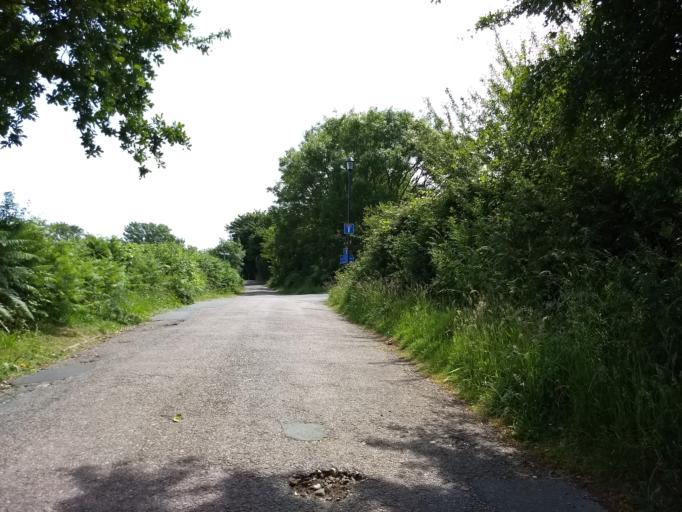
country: GB
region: England
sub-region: Isle of Wight
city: Shanklin
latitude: 50.6177
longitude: -1.1761
